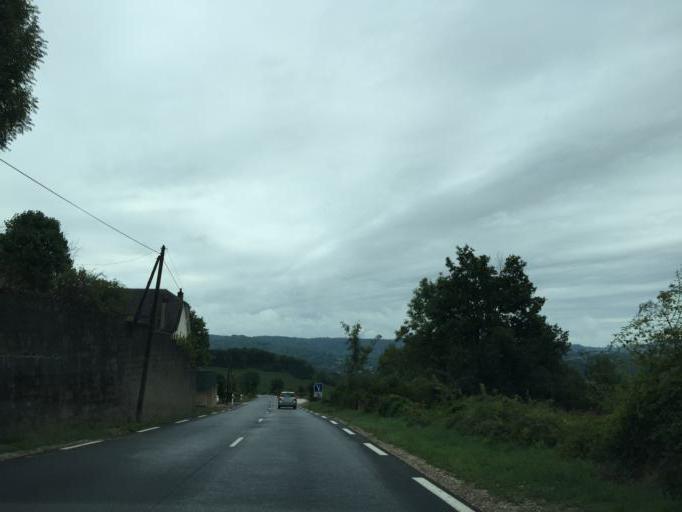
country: FR
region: Midi-Pyrenees
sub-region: Departement de l'Aveyron
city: Espalion
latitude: 44.5373
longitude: 2.7700
